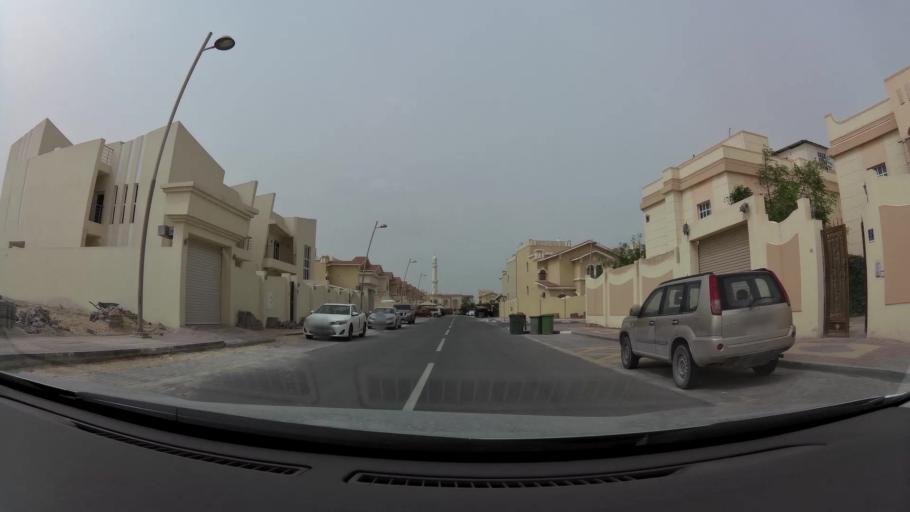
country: QA
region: Baladiyat ad Dawhah
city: Doha
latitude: 25.2277
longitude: 51.5361
